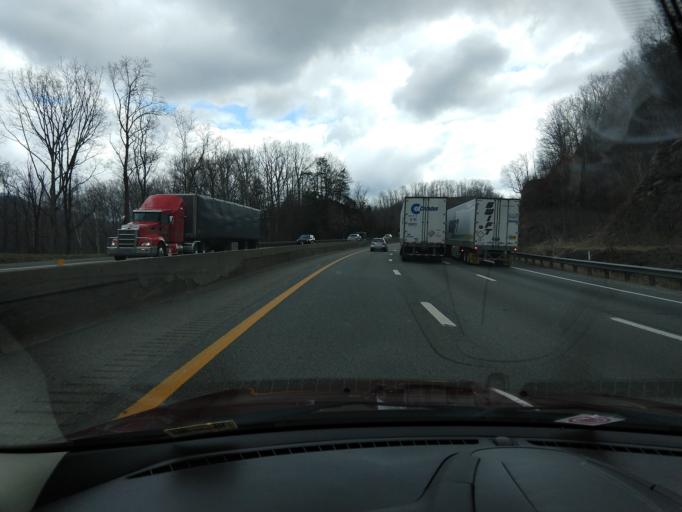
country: US
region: West Virginia
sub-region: Fayette County
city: Oak Hill
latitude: 37.9902
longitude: -81.3246
